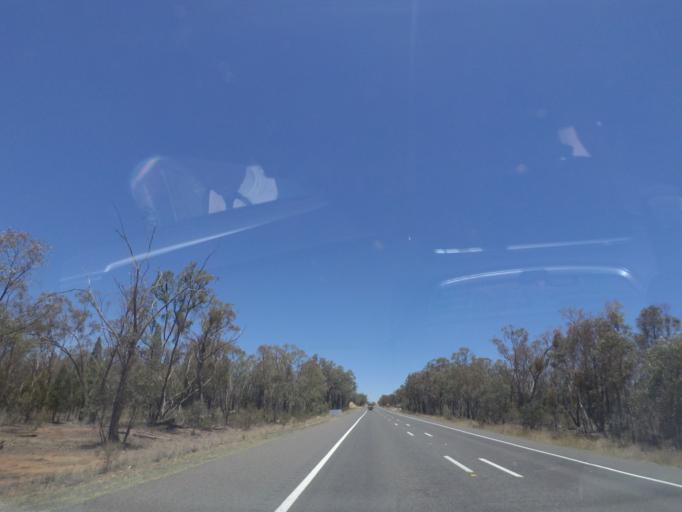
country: AU
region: New South Wales
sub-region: Warrumbungle Shire
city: Coonabarabran
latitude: -30.9159
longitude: 149.4343
